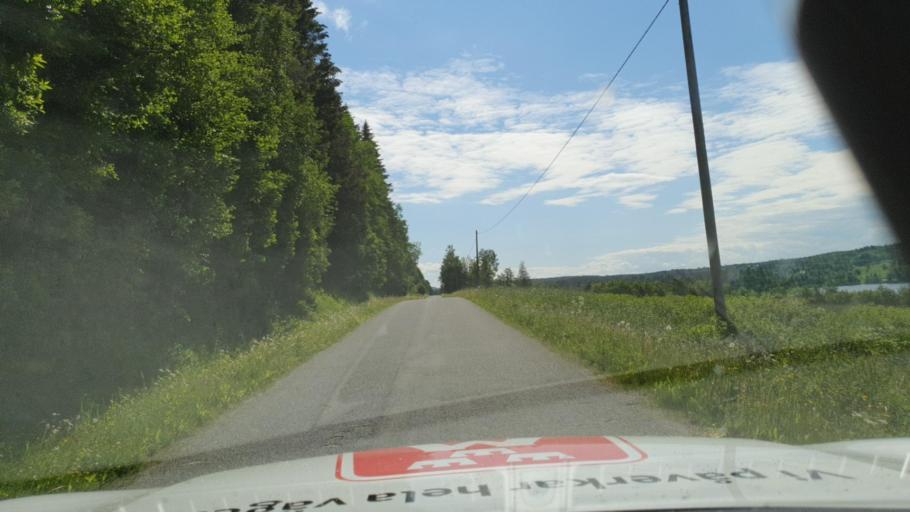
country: SE
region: Jaemtland
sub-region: Bergs Kommun
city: Hoverberg
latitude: 62.8368
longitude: 14.4121
